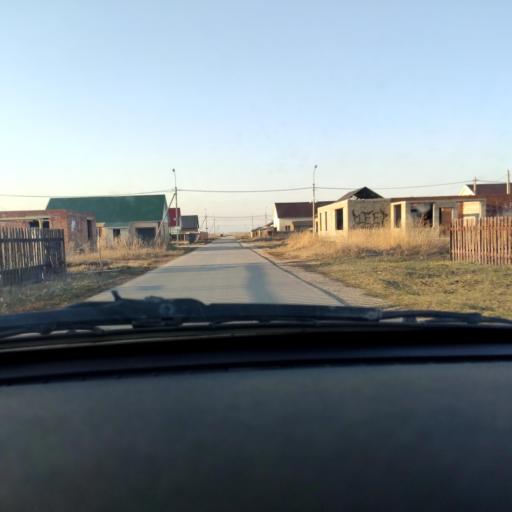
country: RU
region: Samara
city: Podstepki
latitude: 53.5744
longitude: 49.1132
